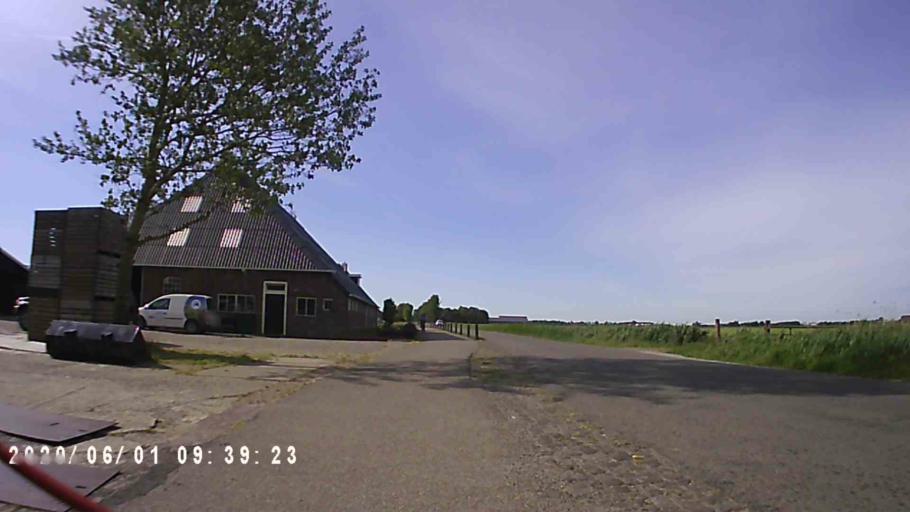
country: NL
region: Friesland
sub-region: Gemeente Het Bildt
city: Sint Annaparochie
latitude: 53.2555
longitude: 5.6806
